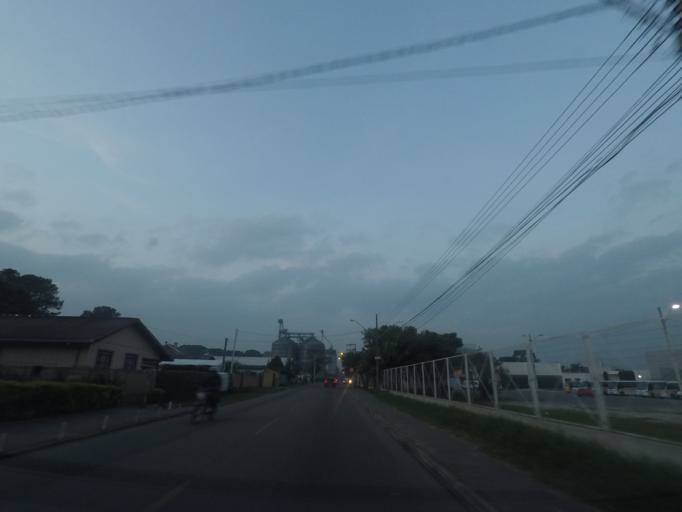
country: BR
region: Parana
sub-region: Pinhais
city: Pinhais
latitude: -25.4490
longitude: -49.1888
